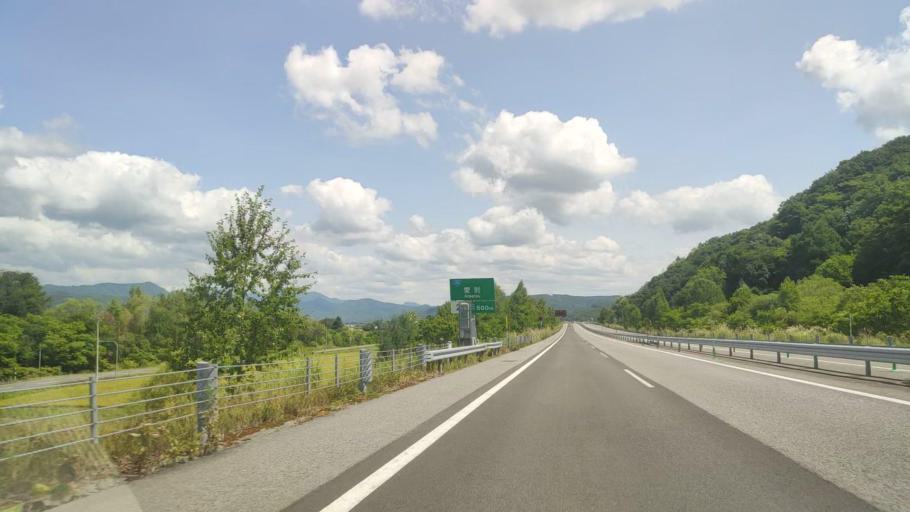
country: JP
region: Hokkaido
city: Kamikawa
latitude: 43.8966
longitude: 142.5629
